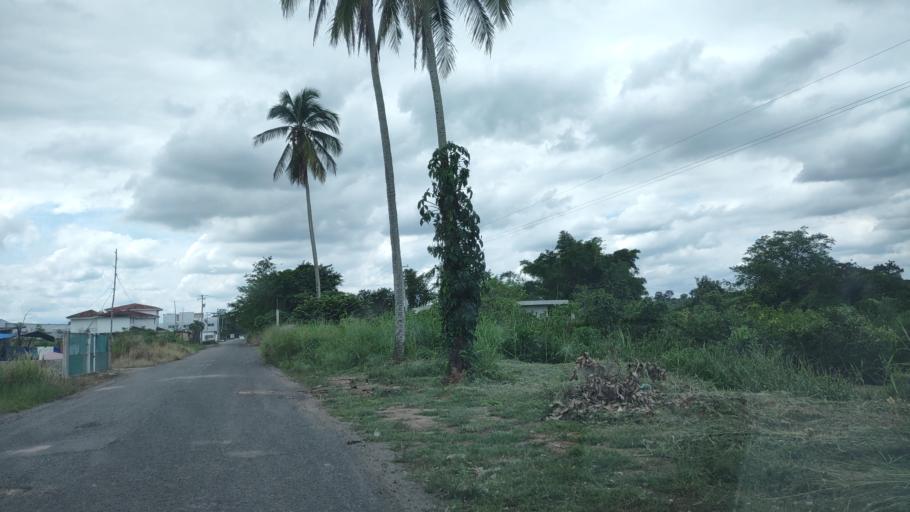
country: MX
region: Veracruz
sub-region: Martinez de la Torre
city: El Progreso
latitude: 20.0989
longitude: -97.0067
